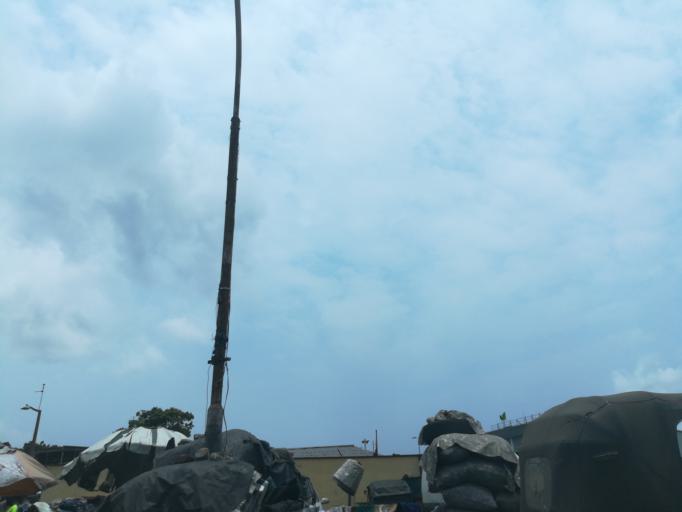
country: NG
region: Lagos
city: Lagos
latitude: 6.4566
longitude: 3.4016
